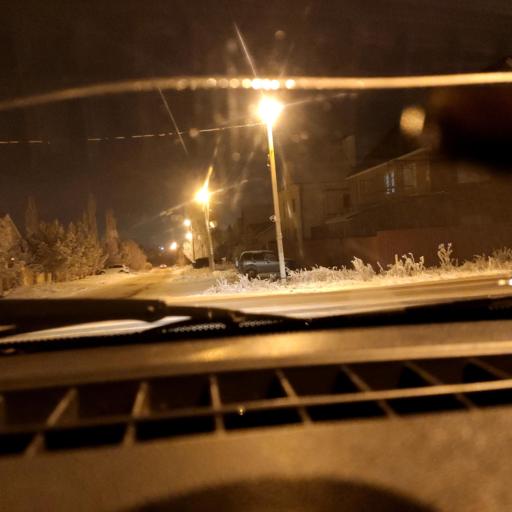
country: RU
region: Bashkortostan
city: Ufa
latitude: 54.6010
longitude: 55.9356
